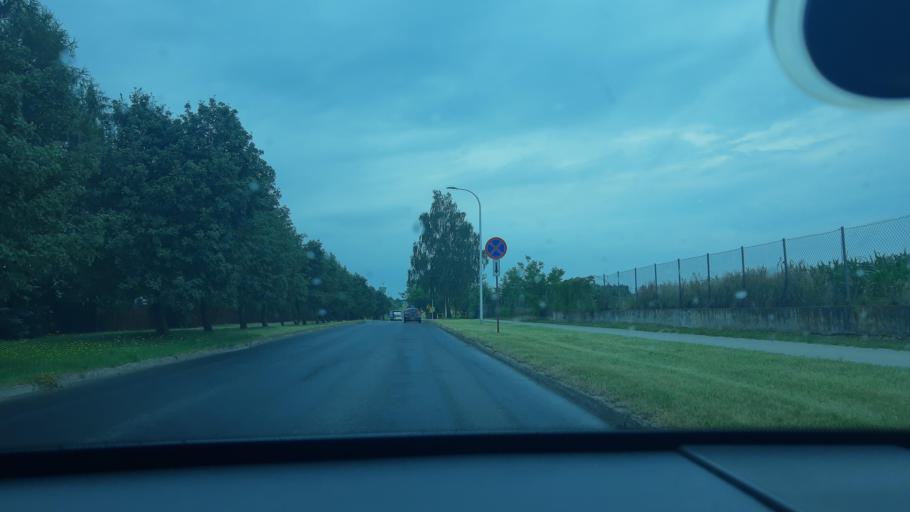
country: PL
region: Lodz Voivodeship
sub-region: Powiat sieradzki
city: Sieradz
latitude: 51.5803
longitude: 18.7067
